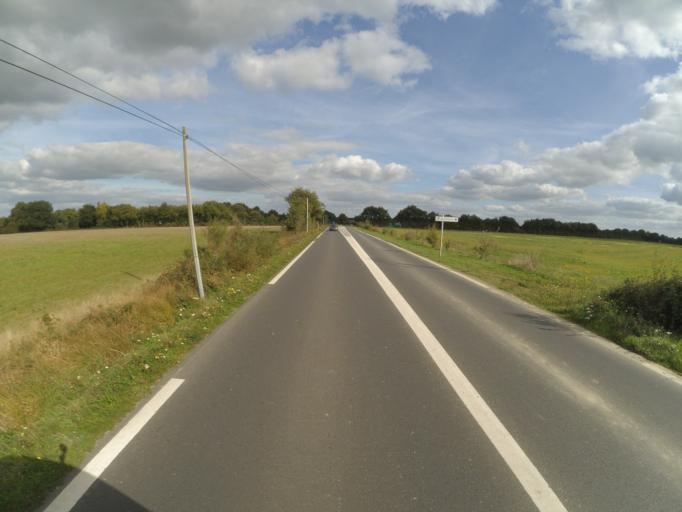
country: FR
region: Pays de la Loire
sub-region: Departement de la Loire-Atlantique
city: Notre-Dame-des-Landes
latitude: 47.4086
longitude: -1.7219
